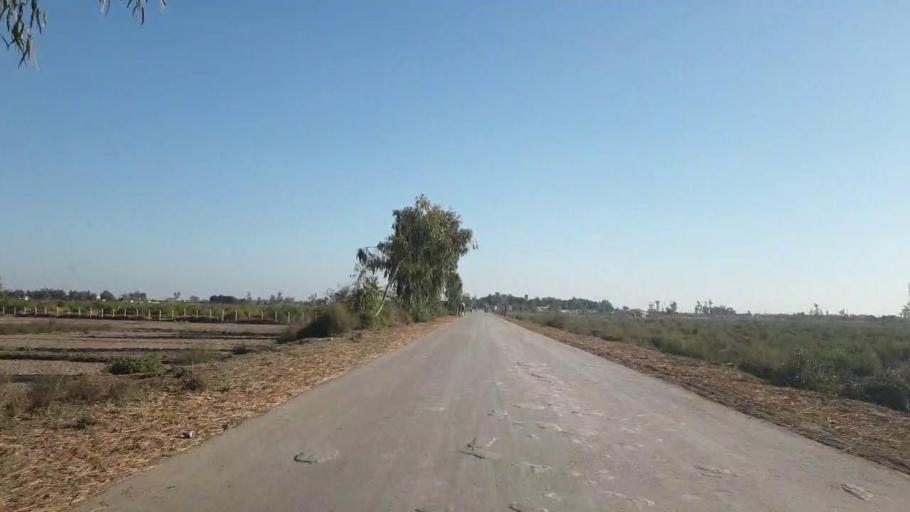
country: PK
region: Sindh
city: Dokri
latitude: 27.3358
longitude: 68.1282
